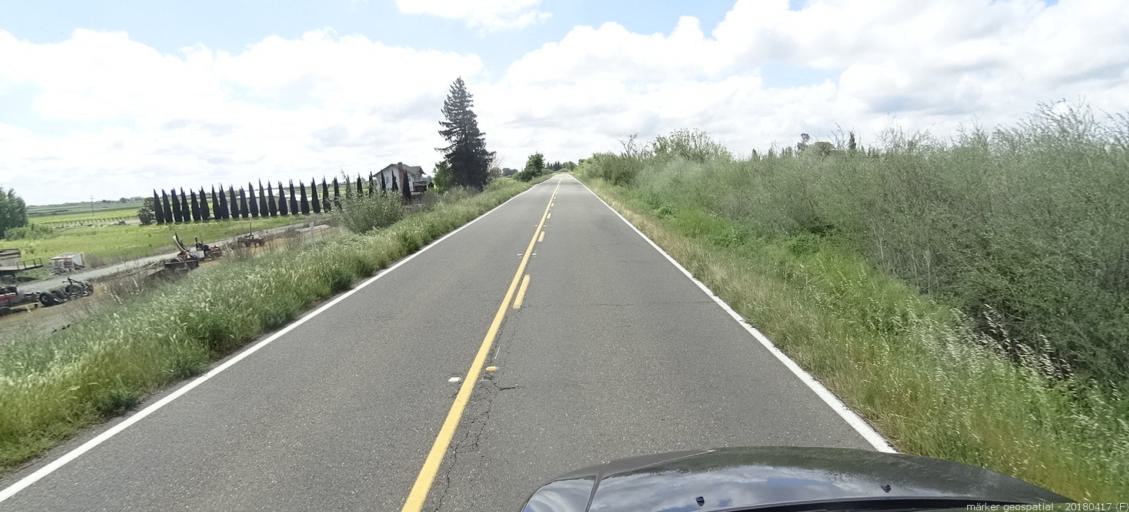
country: US
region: California
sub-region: Sacramento County
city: Walnut Grove
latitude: 38.2146
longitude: -121.5569
